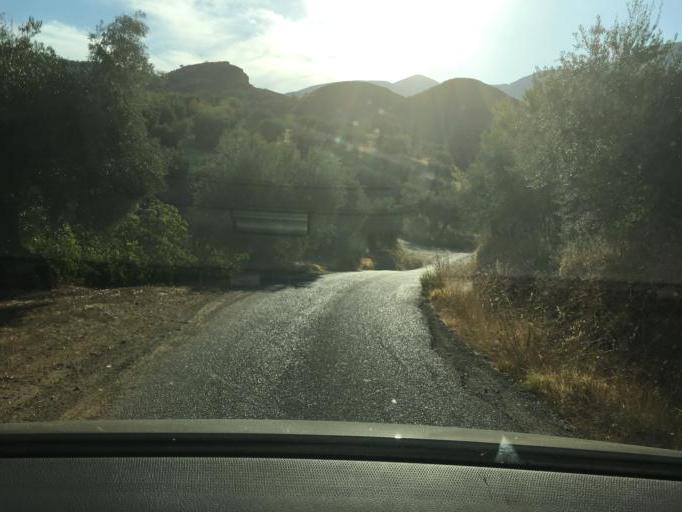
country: ES
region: Andalusia
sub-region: Provincia de Granada
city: Quentar
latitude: 37.1992
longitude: -3.4673
